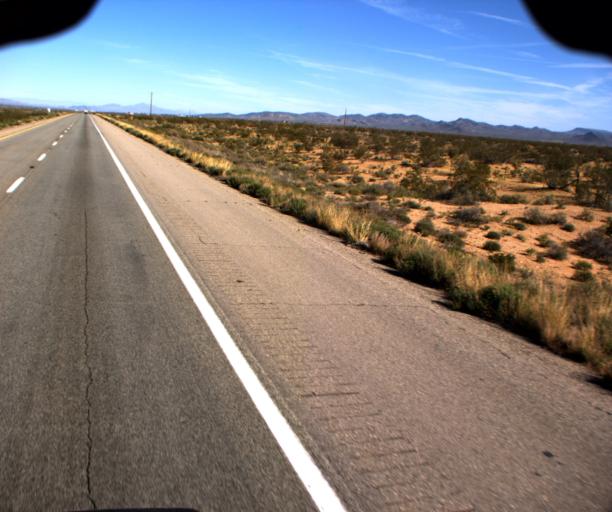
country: US
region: Arizona
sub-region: Mohave County
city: Dolan Springs
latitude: 35.5005
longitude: -114.3320
